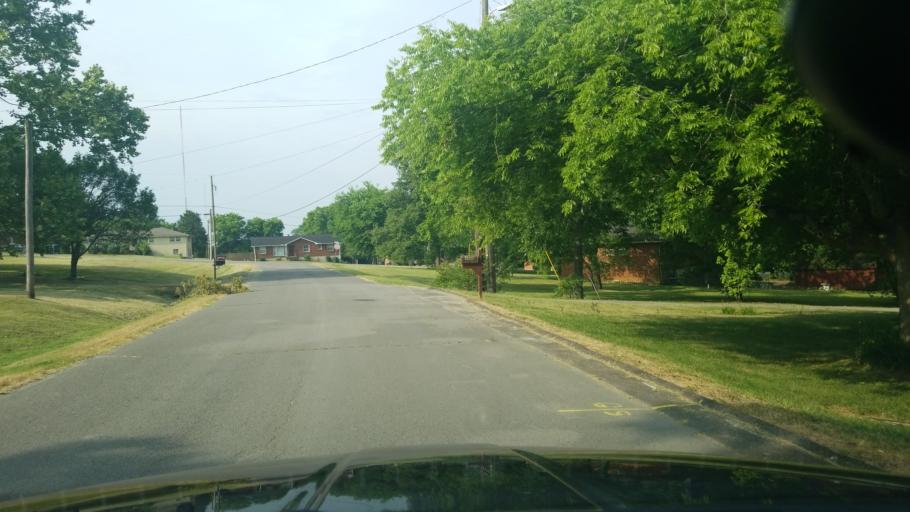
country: US
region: Tennessee
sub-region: Davidson County
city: Goodlettsville
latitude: 36.2759
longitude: -86.7577
